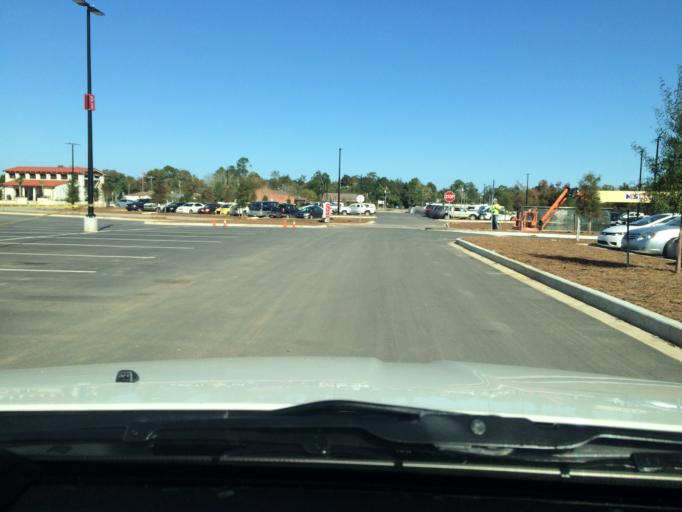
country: US
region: Mississippi
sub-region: Harrison County
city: D'Iberville
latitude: 30.4276
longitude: -88.8892
